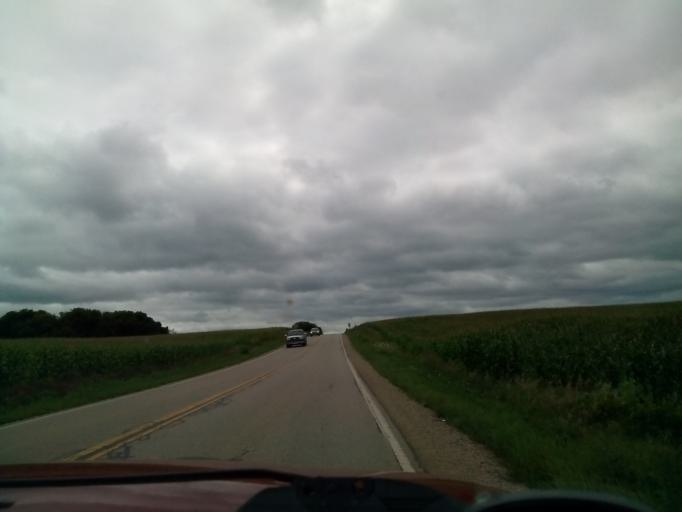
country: US
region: Wisconsin
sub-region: Oconto County
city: Gillett
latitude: 45.0030
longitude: -88.4175
